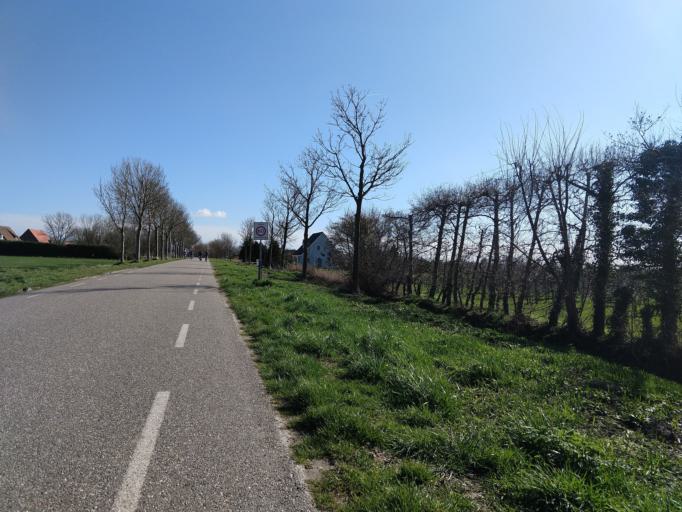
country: NL
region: Zeeland
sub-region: Gemeente Goes
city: Goes
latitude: 51.5136
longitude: 3.9463
